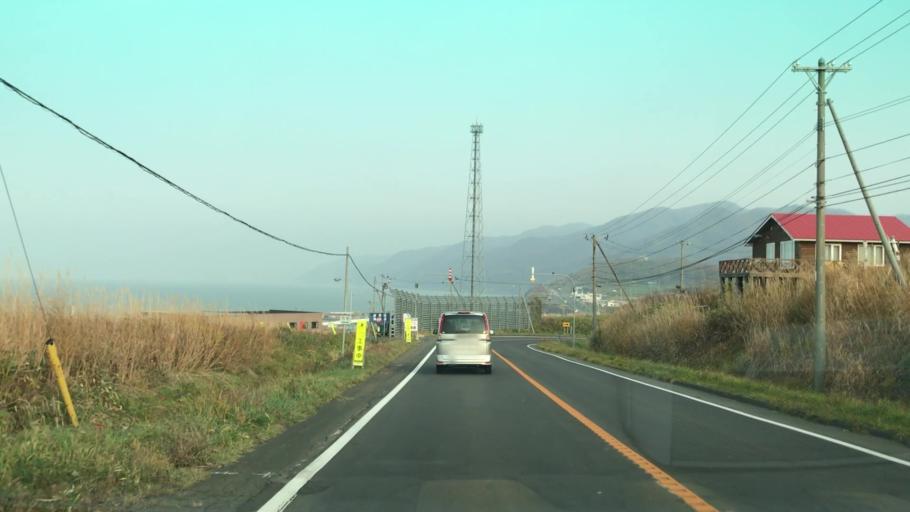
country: JP
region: Hokkaido
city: Ishikari
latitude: 43.3926
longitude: 141.4327
